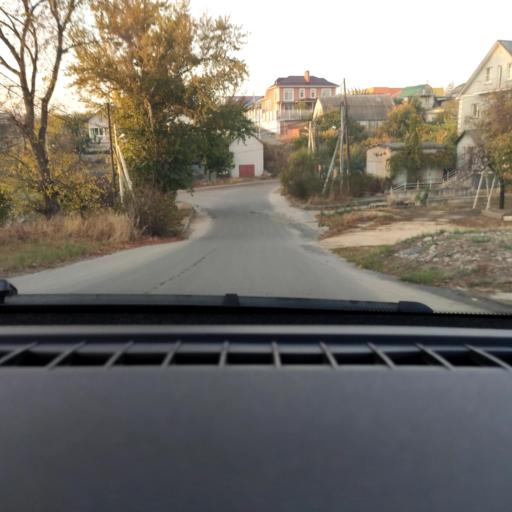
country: RU
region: Voronezj
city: Voronezh
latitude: 51.6304
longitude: 39.1979
